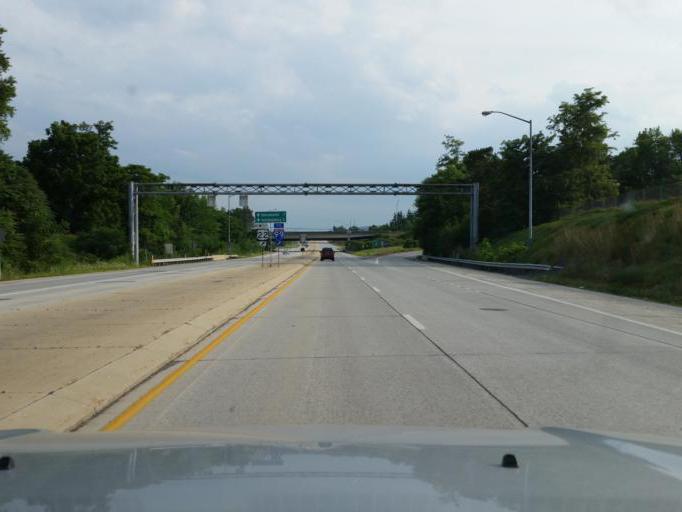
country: US
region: Pennsylvania
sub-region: Blair County
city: Duncansville
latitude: 40.4475
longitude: -78.4327
